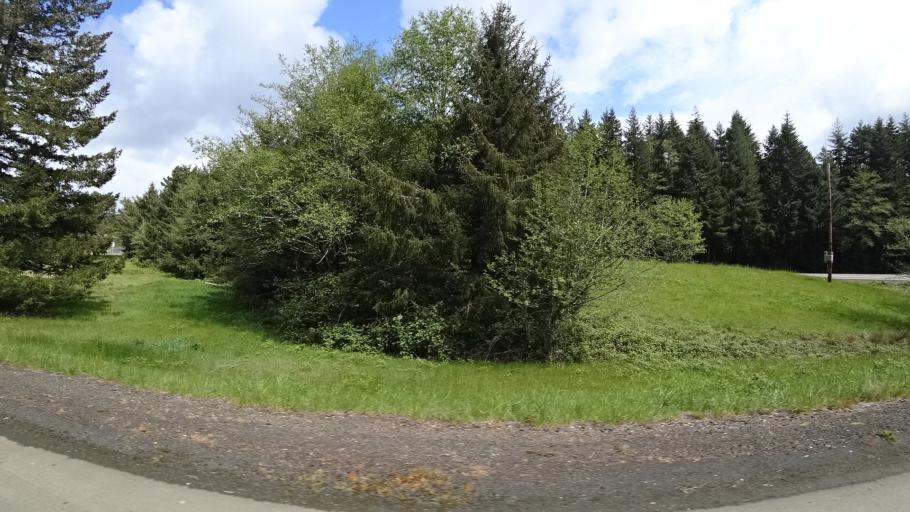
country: US
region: Oregon
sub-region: Lincoln County
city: Lincoln City
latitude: 45.0180
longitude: -123.9761
